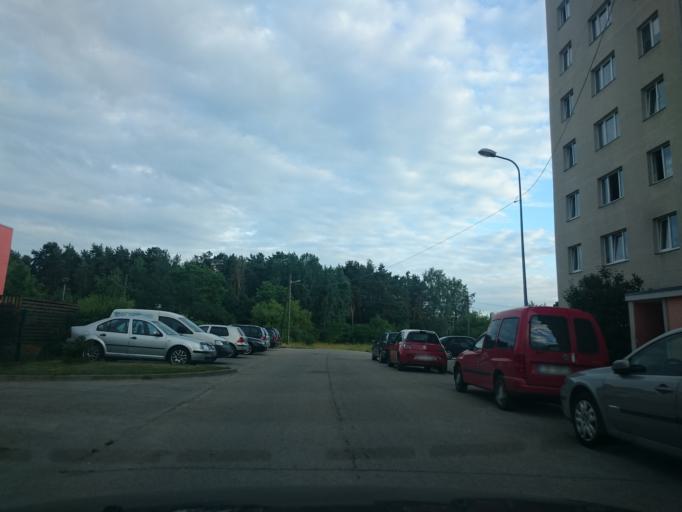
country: LV
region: Stopini
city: Ulbroka
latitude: 56.9459
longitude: 24.2335
